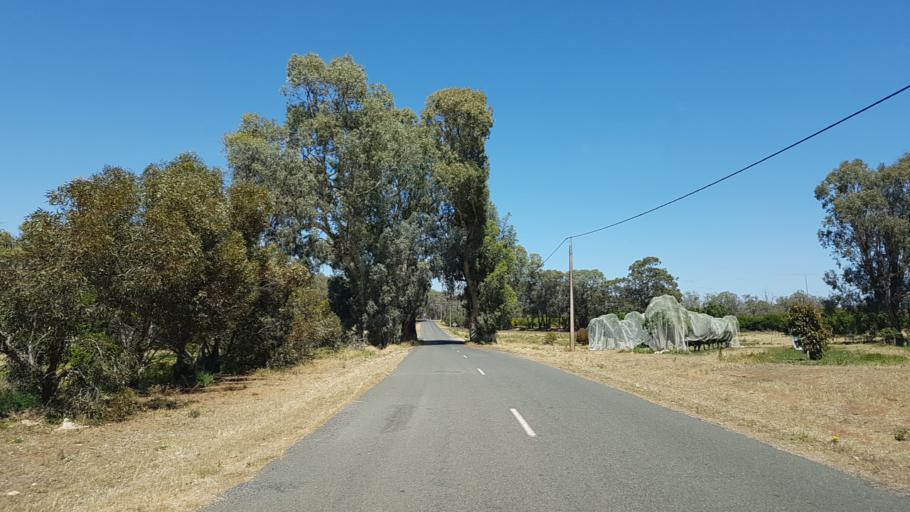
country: AU
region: South Australia
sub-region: Loxton Waikerie
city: Waikerie
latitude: -34.1652
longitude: 140.0292
